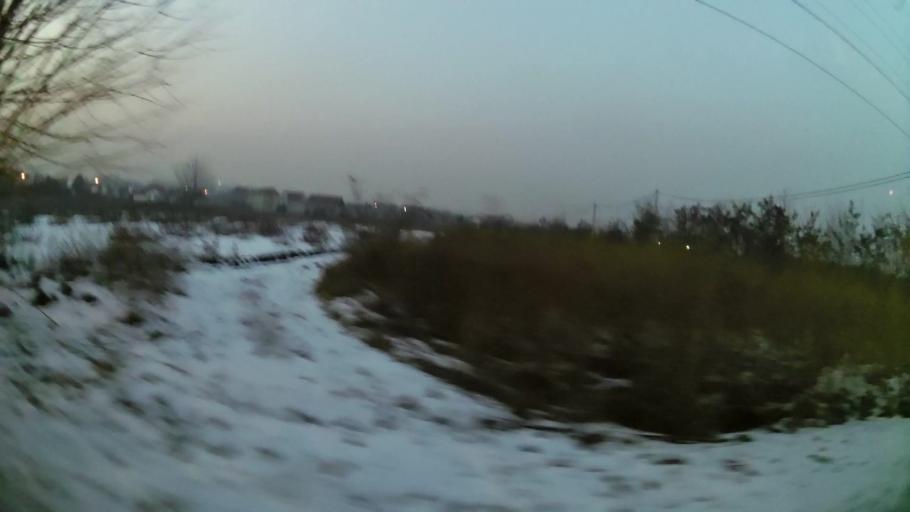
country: MK
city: Creshevo
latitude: 42.0058
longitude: 21.5144
